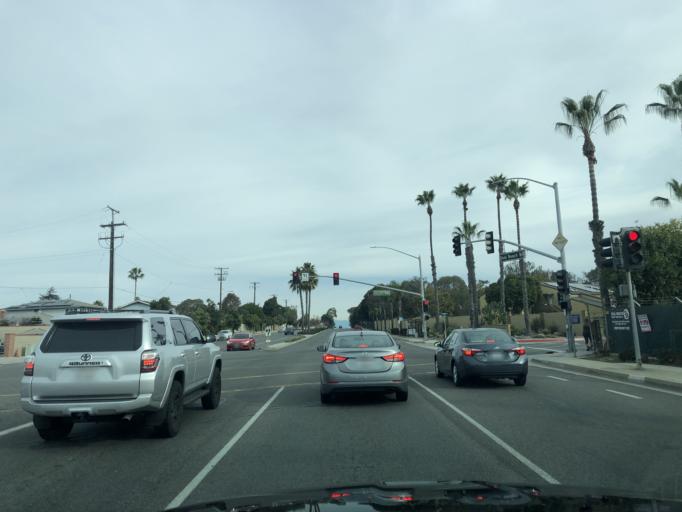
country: US
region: California
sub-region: Orange County
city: Seal Beach
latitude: 33.7445
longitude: -118.0927
